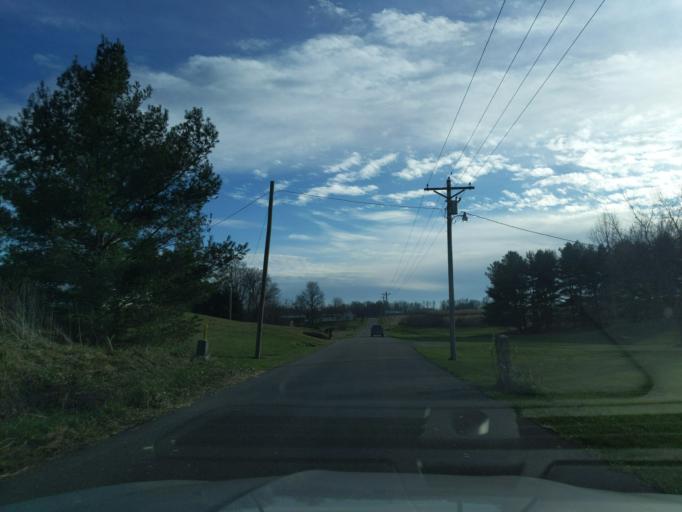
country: US
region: Indiana
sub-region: Decatur County
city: Westport
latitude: 39.1873
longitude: -85.5456
